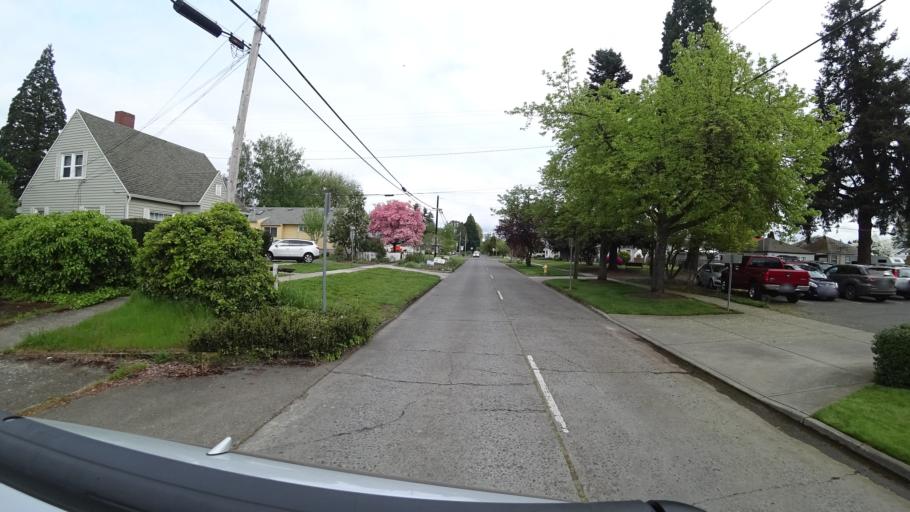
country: US
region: Oregon
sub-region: Washington County
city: Hillsboro
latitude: 45.5230
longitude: -122.9826
